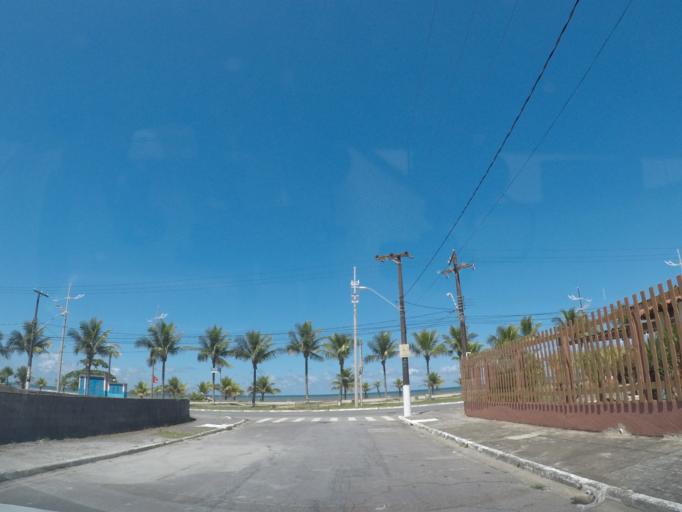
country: BR
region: Sao Paulo
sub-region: Mongagua
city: Mongagua
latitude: -24.0733
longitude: -46.5739
